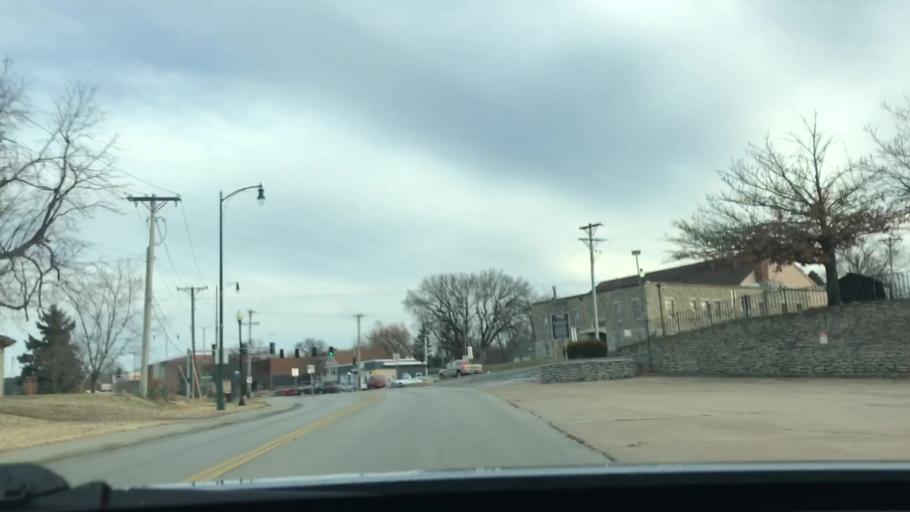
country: US
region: Missouri
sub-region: Jackson County
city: Sugar Creek
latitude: 39.0882
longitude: -94.4517
